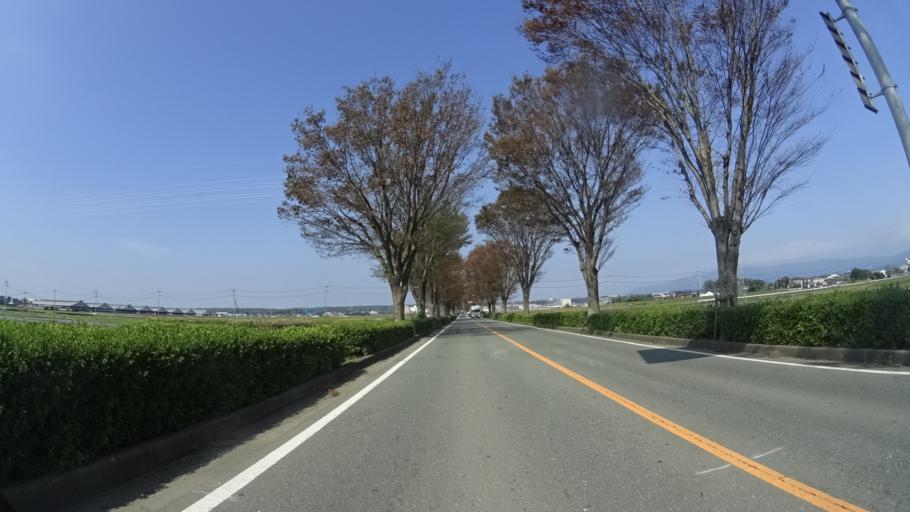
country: JP
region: Kumamoto
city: Ozu
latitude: 32.8603
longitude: 130.8553
